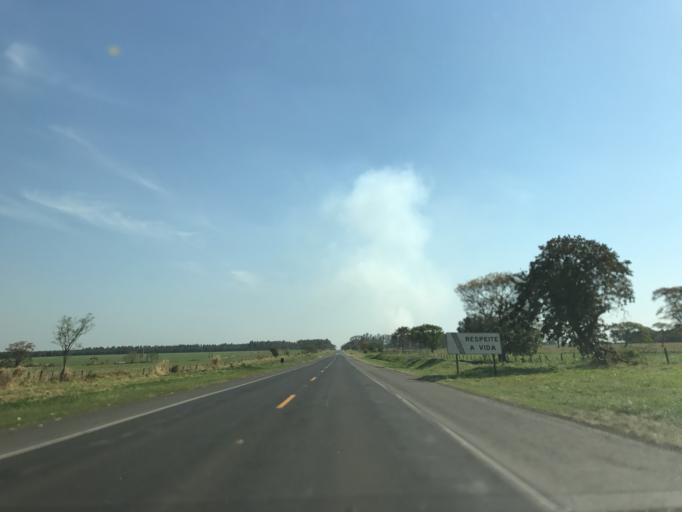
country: BR
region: Sao Paulo
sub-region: Penapolis
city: Penapolis
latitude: -21.3677
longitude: -50.0756
